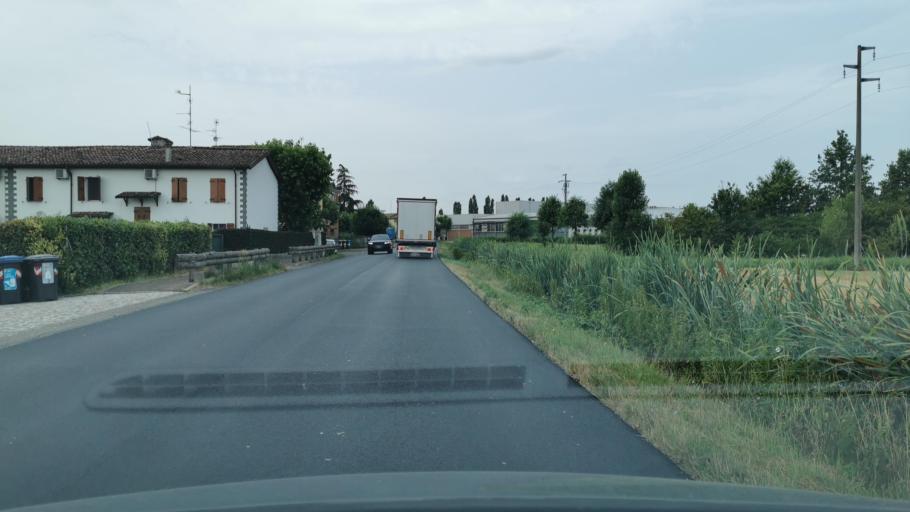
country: IT
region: Emilia-Romagna
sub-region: Provincia di Modena
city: Villanova
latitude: 44.6997
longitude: 10.8928
